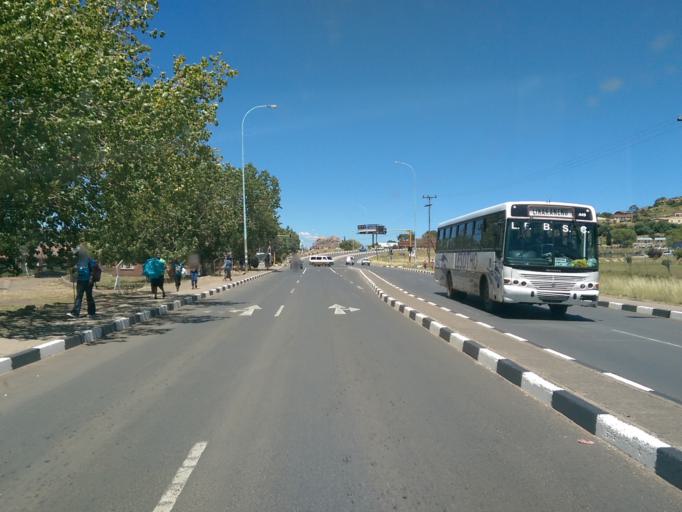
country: LS
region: Maseru
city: Maseru
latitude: -29.3231
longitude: 27.4991
